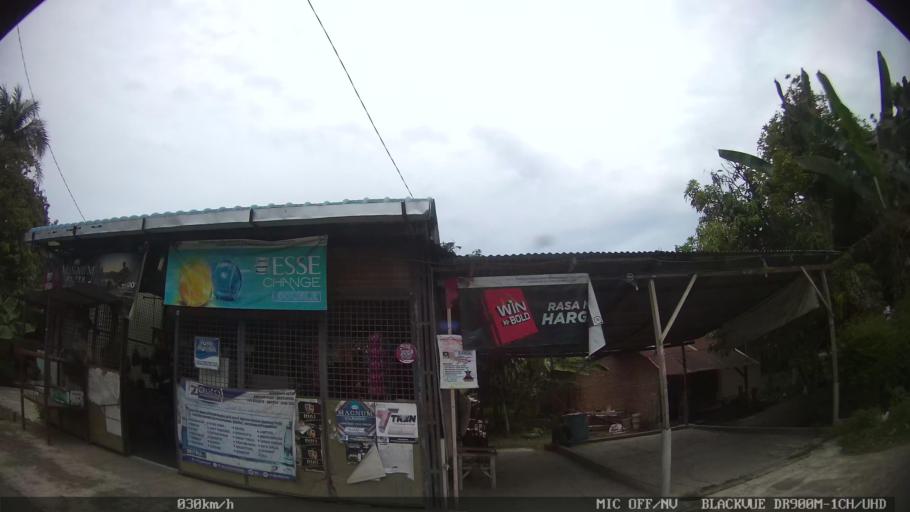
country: ID
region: North Sumatra
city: Binjai
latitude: 3.6448
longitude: 98.5509
